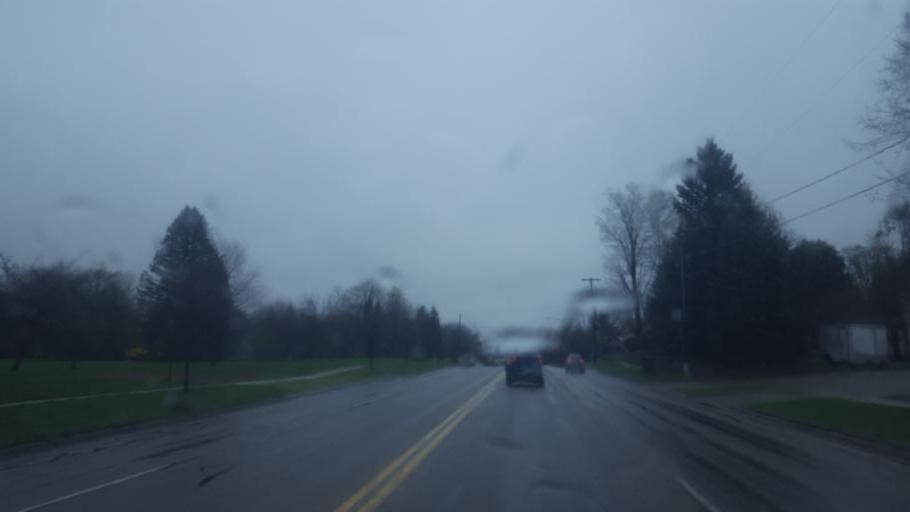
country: US
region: Michigan
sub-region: Isabella County
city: Mount Pleasant
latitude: 43.6117
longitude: -84.7920
